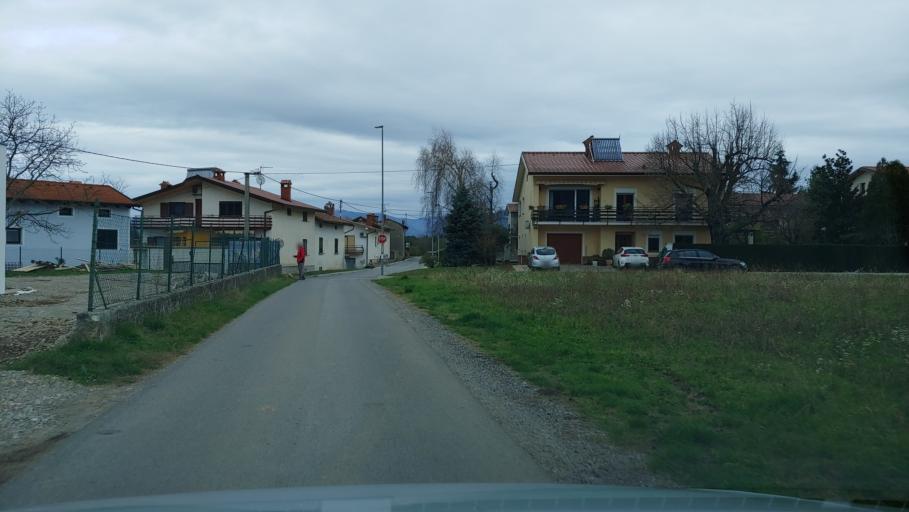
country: SI
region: Miren-Kostanjevica
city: Miren
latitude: 45.8919
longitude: 13.6144
